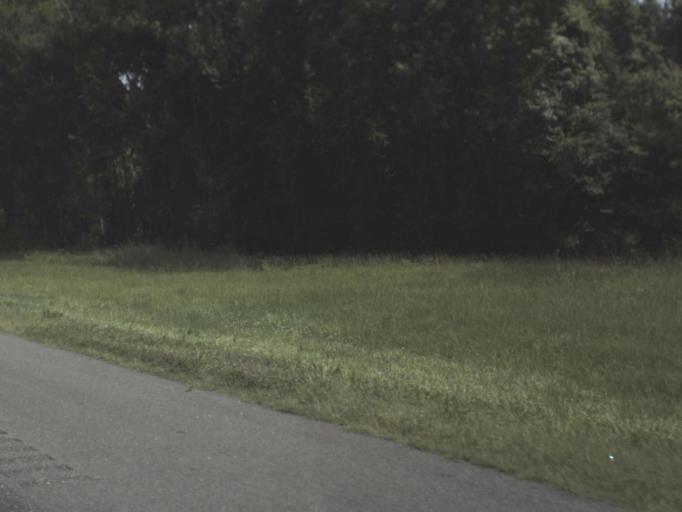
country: US
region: Florida
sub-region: Hamilton County
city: Jasper
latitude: 30.5244
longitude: -83.0658
